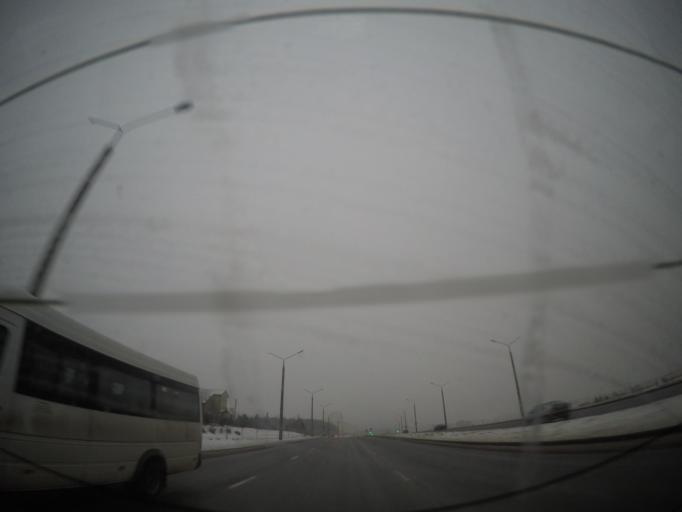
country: BY
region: Grodnenskaya
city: Hrodna
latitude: 53.6288
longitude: 23.8044
